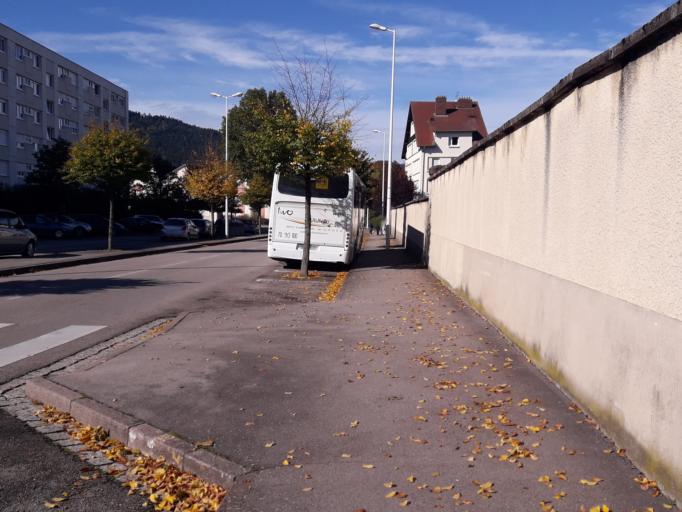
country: FR
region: Lorraine
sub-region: Departement des Vosges
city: Saint-Die-des-Vosges
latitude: 48.2834
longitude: 6.9590
